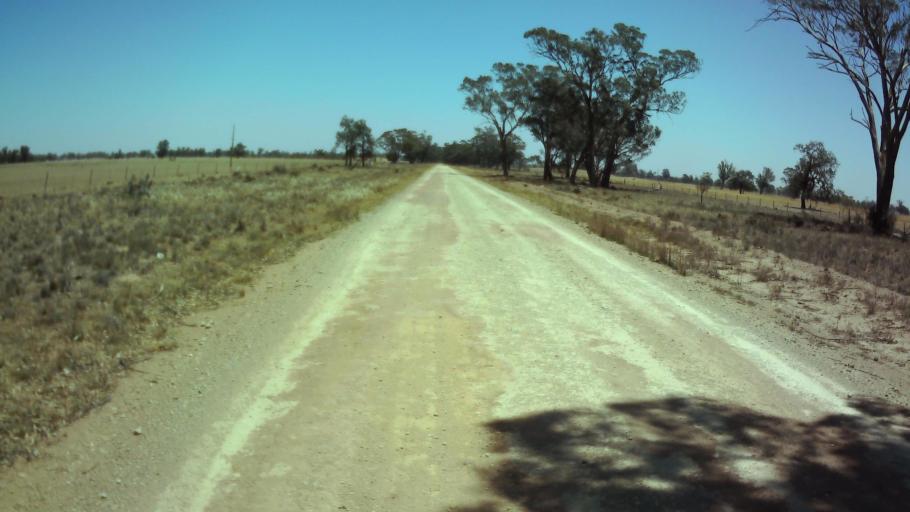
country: AU
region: New South Wales
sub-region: Weddin
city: Grenfell
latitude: -34.0299
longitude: 147.8697
